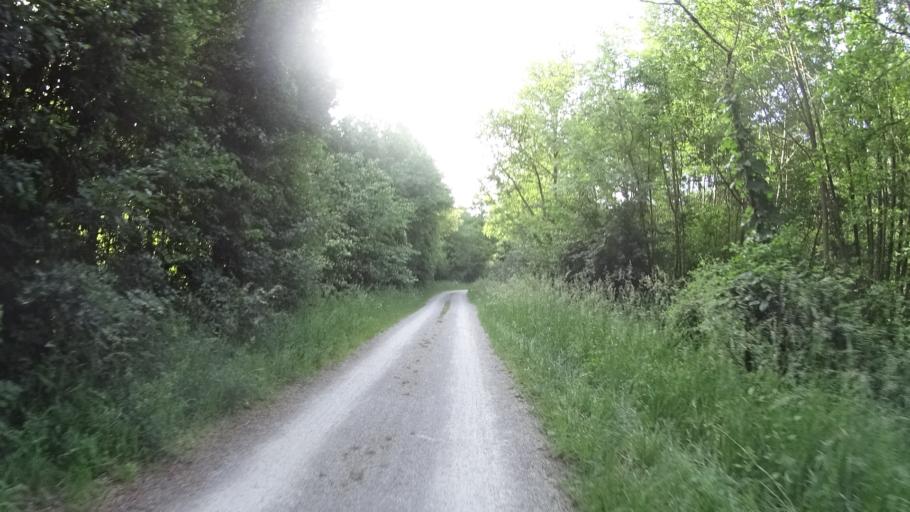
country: DE
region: Bavaria
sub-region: Lower Bavaria
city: Essing
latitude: 48.9457
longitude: 11.7432
